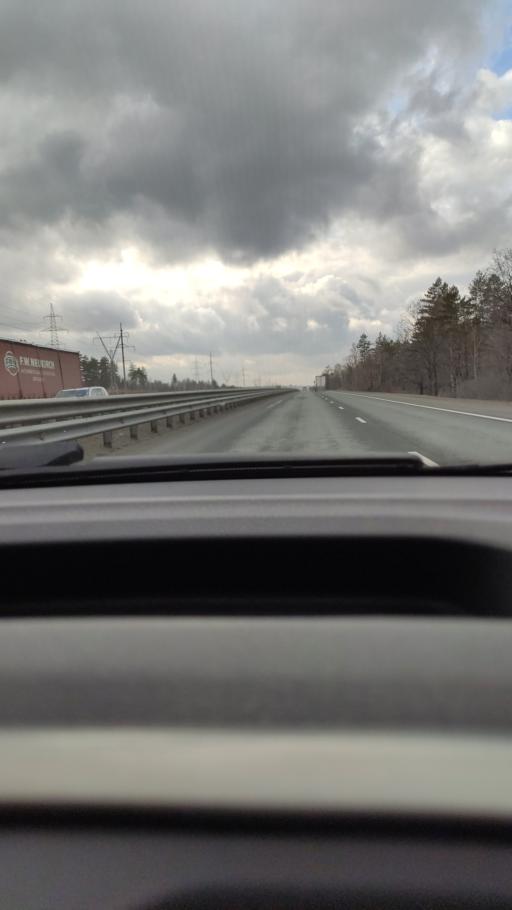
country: RU
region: Samara
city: Povolzhskiy
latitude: 53.5168
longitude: 49.7178
